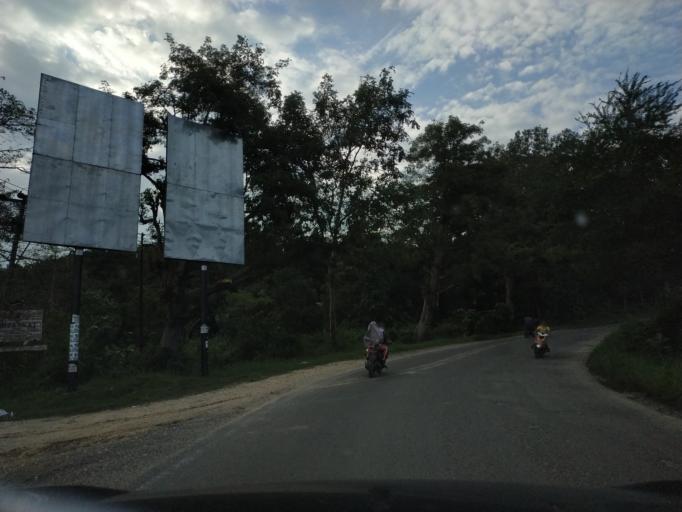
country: ID
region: Central Java
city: Ngampel
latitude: -6.8997
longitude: 111.4398
